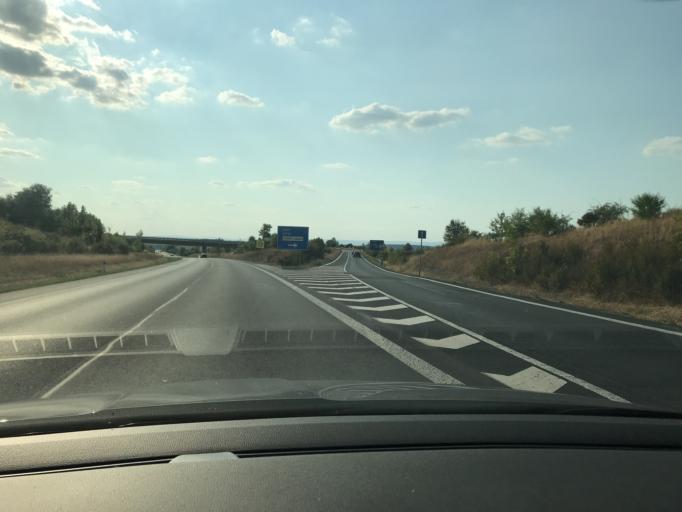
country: CZ
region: Ustecky
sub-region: Okres Louny
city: Louny
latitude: 50.3492
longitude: 13.7757
